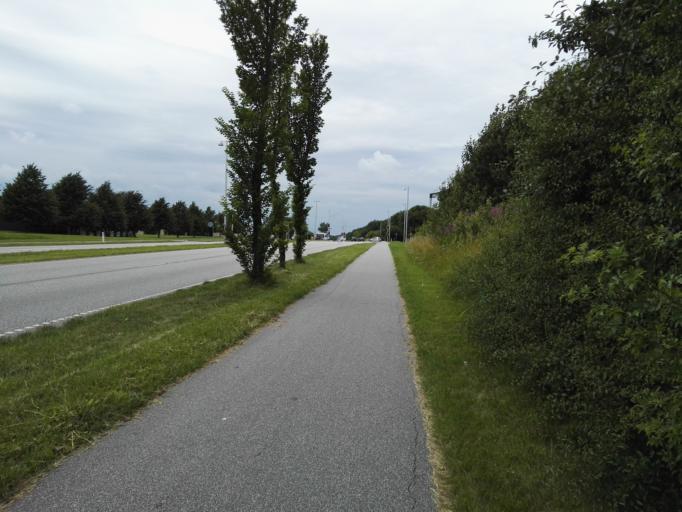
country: DK
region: Capital Region
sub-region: Egedal Kommune
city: Smorumnedre
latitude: 55.7525
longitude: 12.3022
